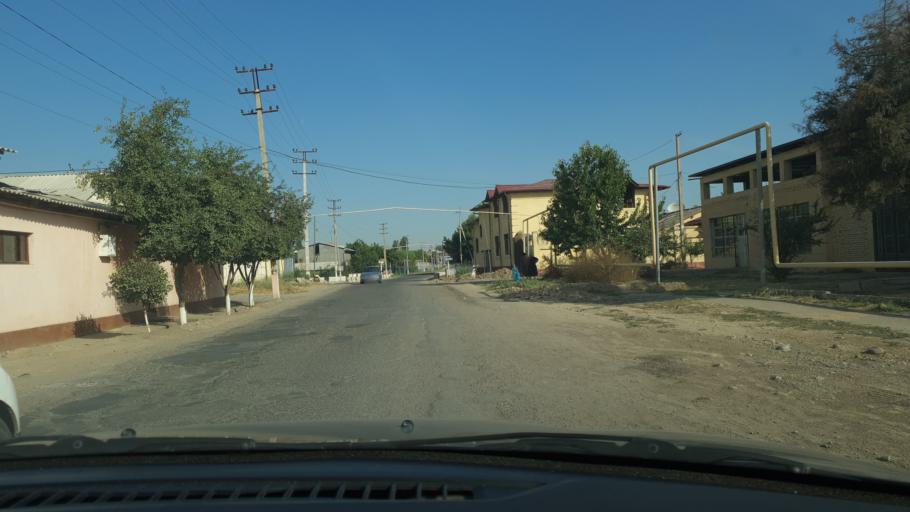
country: UZ
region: Toshkent
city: Urtaowul
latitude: 41.2032
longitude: 69.1529
